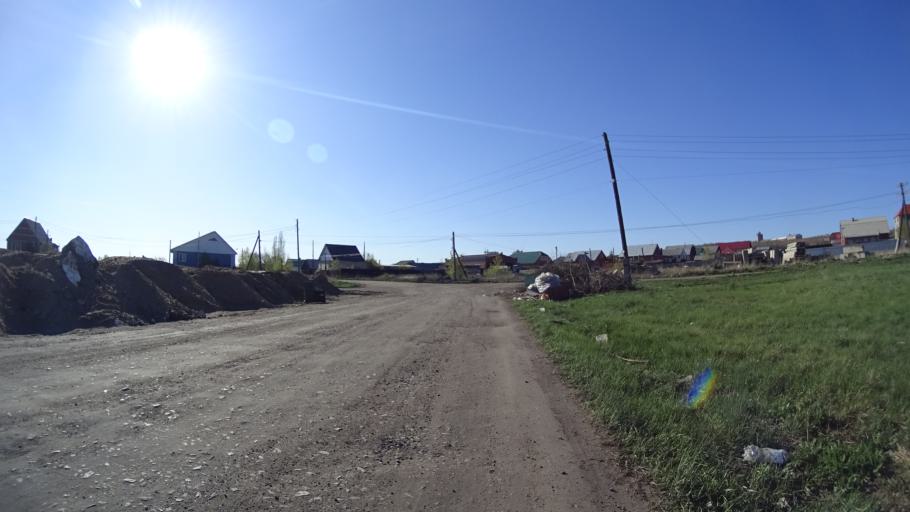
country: RU
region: Chelyabinsk
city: Troitsk
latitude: 54.0958
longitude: 61.5979
